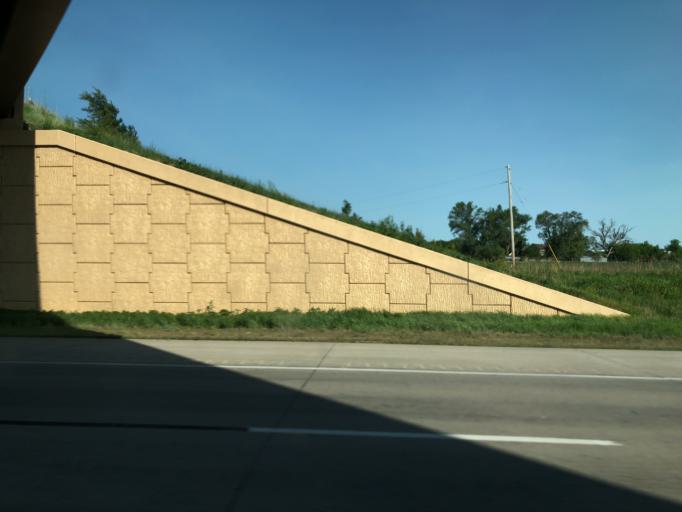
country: US
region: Nebraska
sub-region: Saunders County
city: Ashland
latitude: 40.9572
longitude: -96.4101
